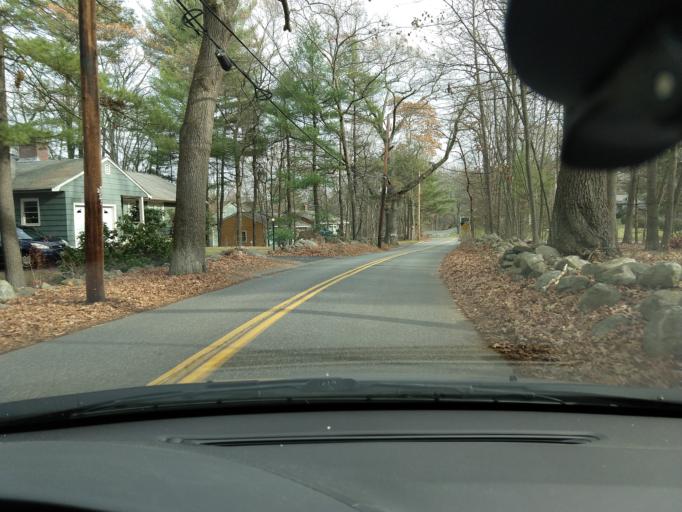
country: US
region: Massachusetts
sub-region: Middlesex County
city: Bedford
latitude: 42.4962
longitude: -71.2501
